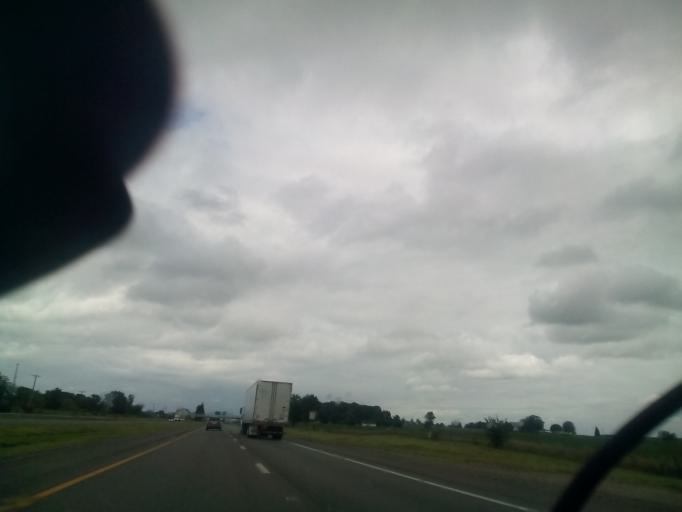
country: US
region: Indiana
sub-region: Steuben County
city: Hamilton
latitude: 41.6297
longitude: -84.7967
